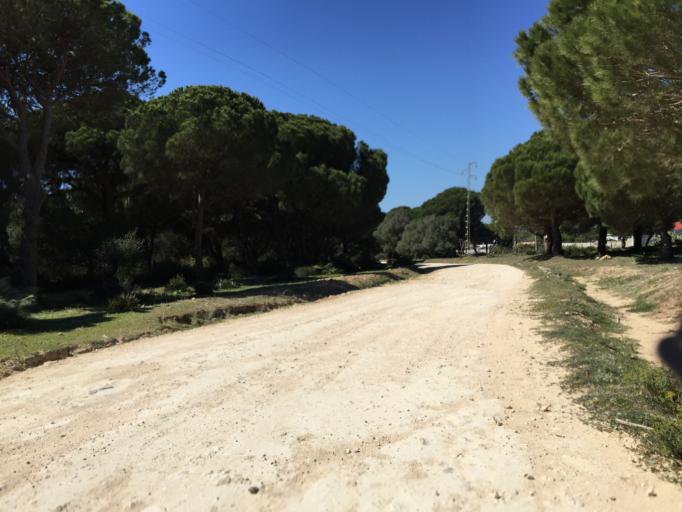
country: ES
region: Andalusia
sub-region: Provincia de Cadiz
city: Vejer de la Frontera
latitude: 36.2050
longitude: -5.9765
